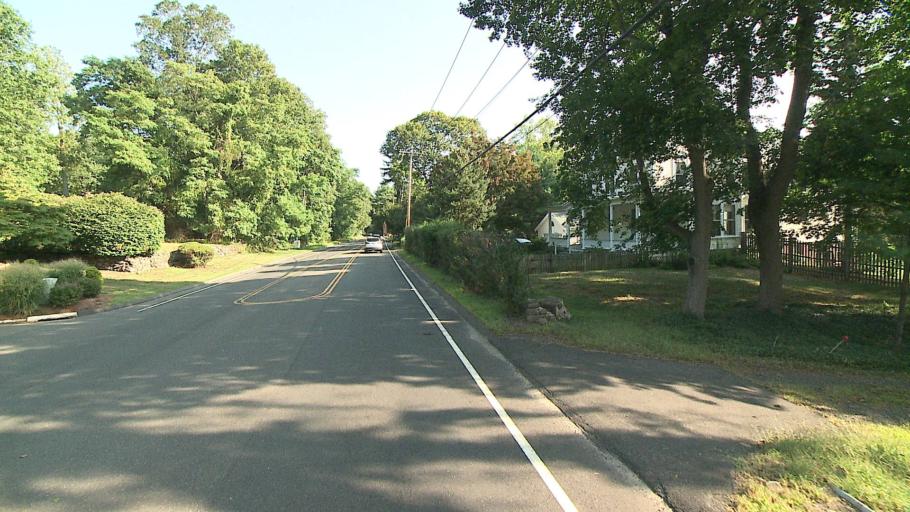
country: US
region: Connecticut
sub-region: New Haven County
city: New Haven
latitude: 41.3098
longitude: -72.9701
